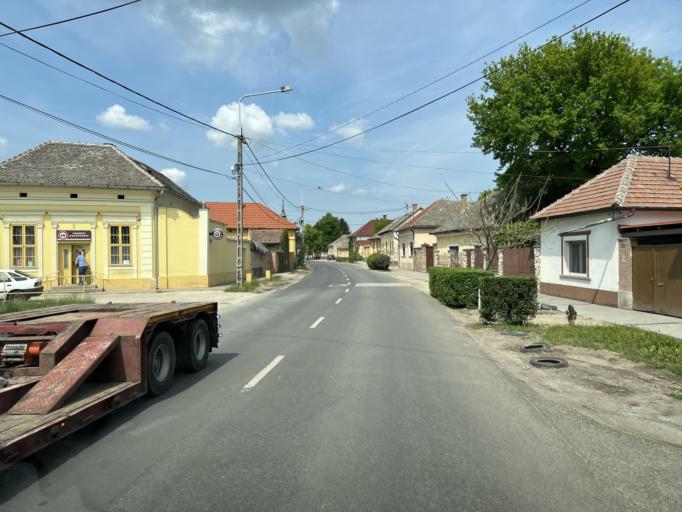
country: HU
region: Pest
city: Nagykoros
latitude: 47.0311
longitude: 19.7906
